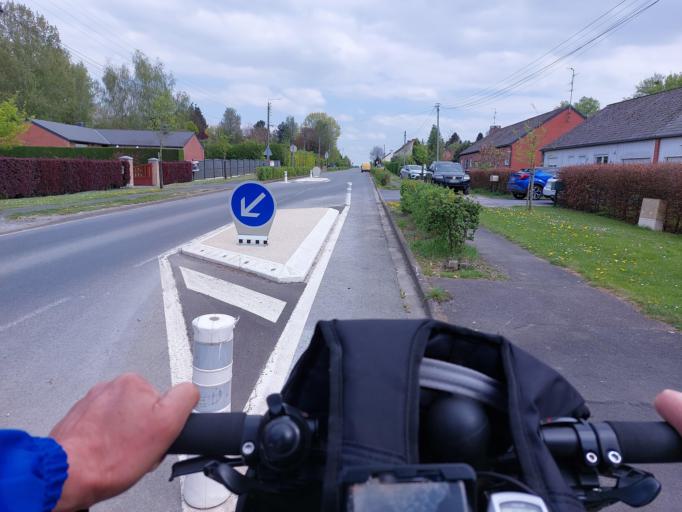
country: FR
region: Nord-Pas-de-Calais
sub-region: Departement du Nord
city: La Longueville
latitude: 50.2856
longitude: 3.8653
